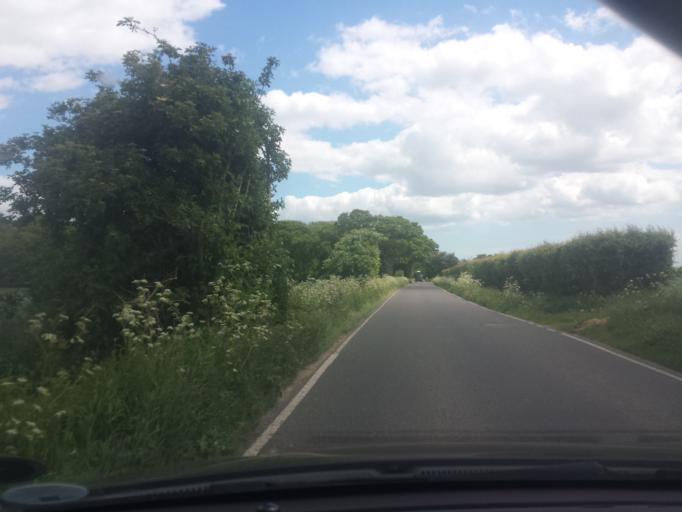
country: GB
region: England
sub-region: Essex
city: Little Clacton
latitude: 51.8884
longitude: 1.1558
